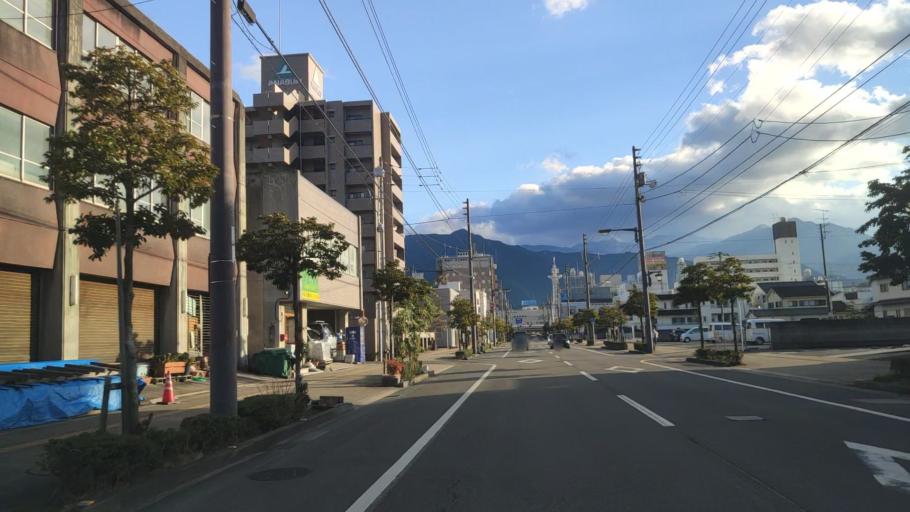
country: JP
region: Ehime
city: Saijo
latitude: 33.9154
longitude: 133.1865
